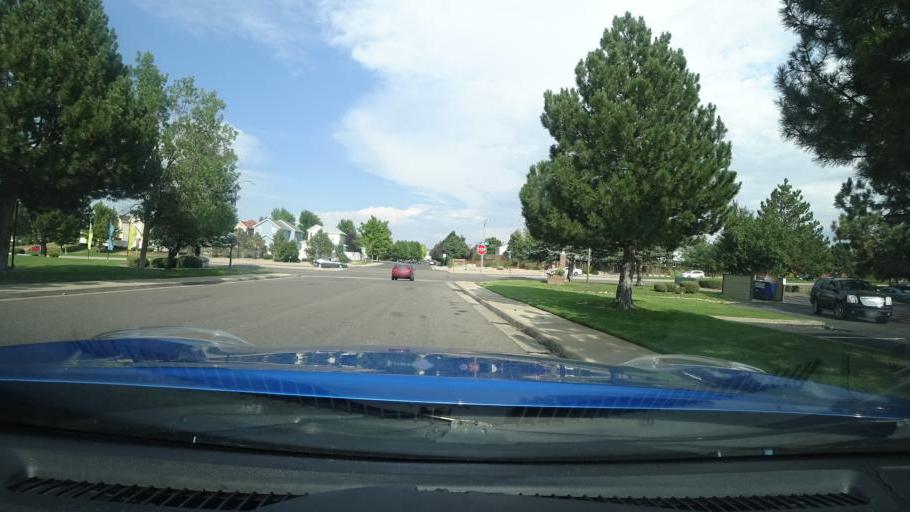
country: US
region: Colorado
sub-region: Adams County
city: Aurora
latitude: 39.6921
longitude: -104.7916
